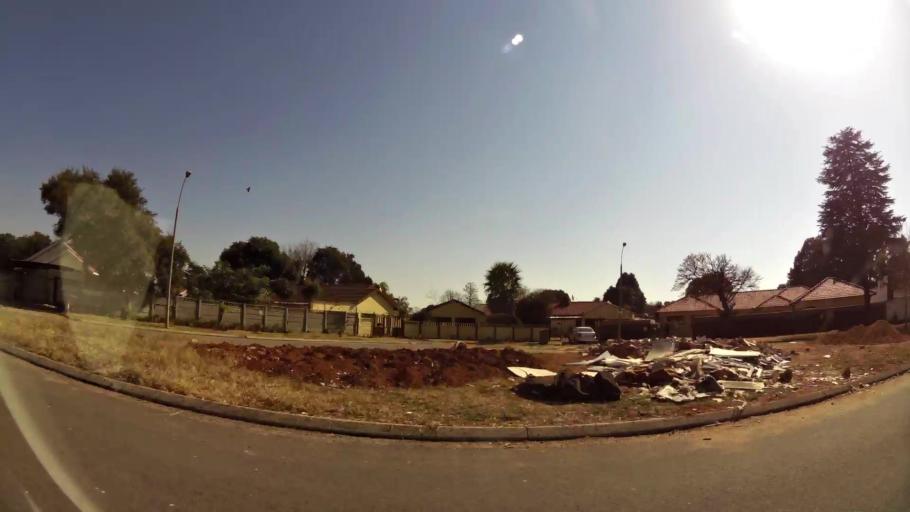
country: ZA
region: Gauteng
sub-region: City of Johannesburg Metropolitan Municipality
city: Modderfontein
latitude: -26.0501
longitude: 28.2041
